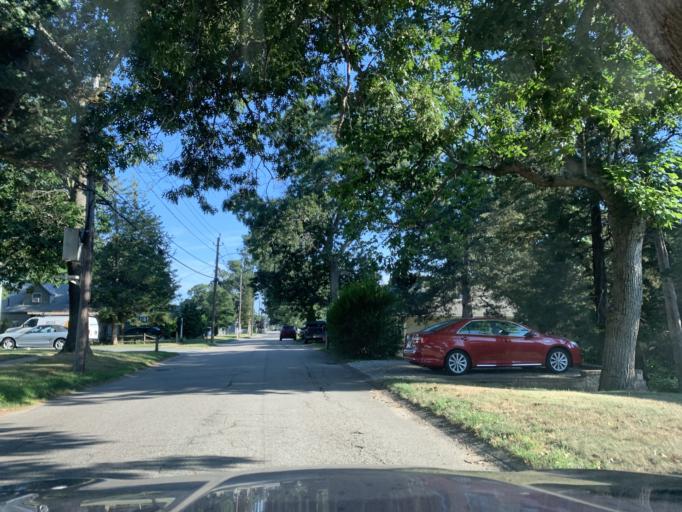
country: US
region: Rhode Island
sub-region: Kent County
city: Warwick
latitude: 41.6926
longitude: -71.4385
